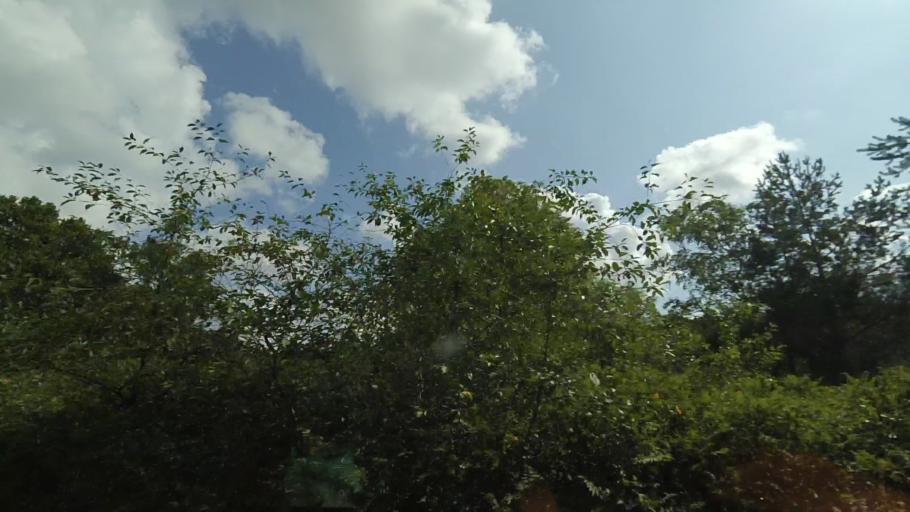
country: DK
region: Central Jutland
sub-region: Norddjurs Kommune
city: Allingabro
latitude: 56.5102
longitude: 10.3955
